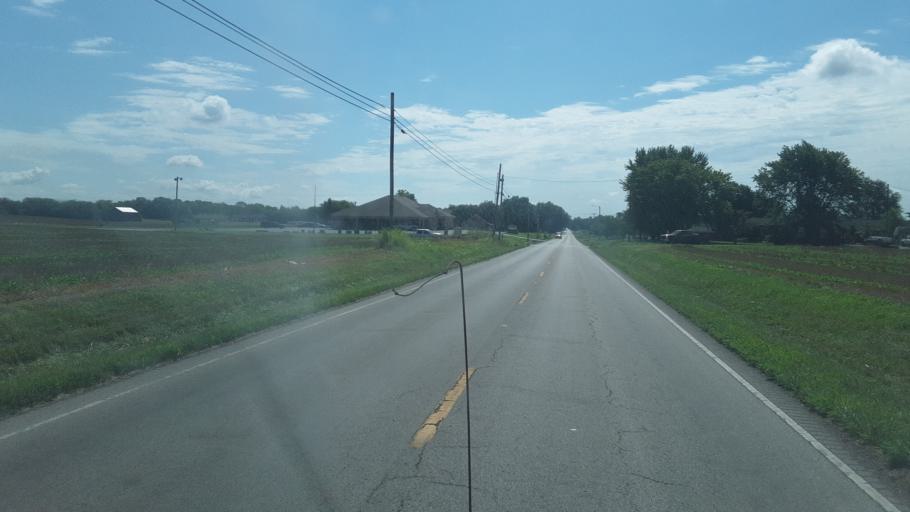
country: US
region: Kentucky
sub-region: Todd County
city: Elkton
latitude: 36.8152
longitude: -87.1783
